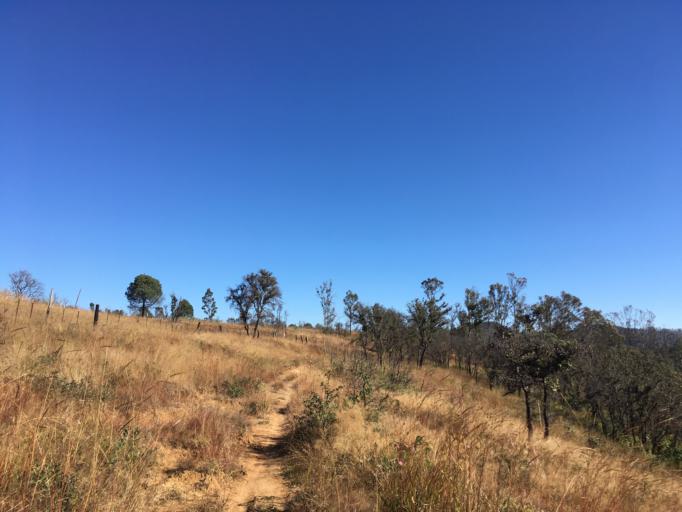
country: MX
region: Michoacan
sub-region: Morelia
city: Montana Monarca (Punta Altozano)
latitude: 19.6619
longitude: -101.1462
